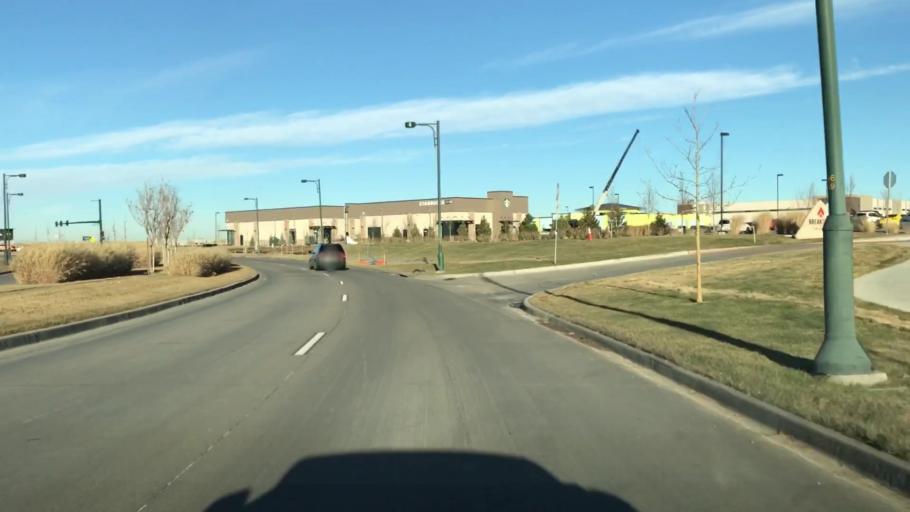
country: US
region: Colorado
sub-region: Adams County
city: Commerce City
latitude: 39.7723
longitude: -104.8836
